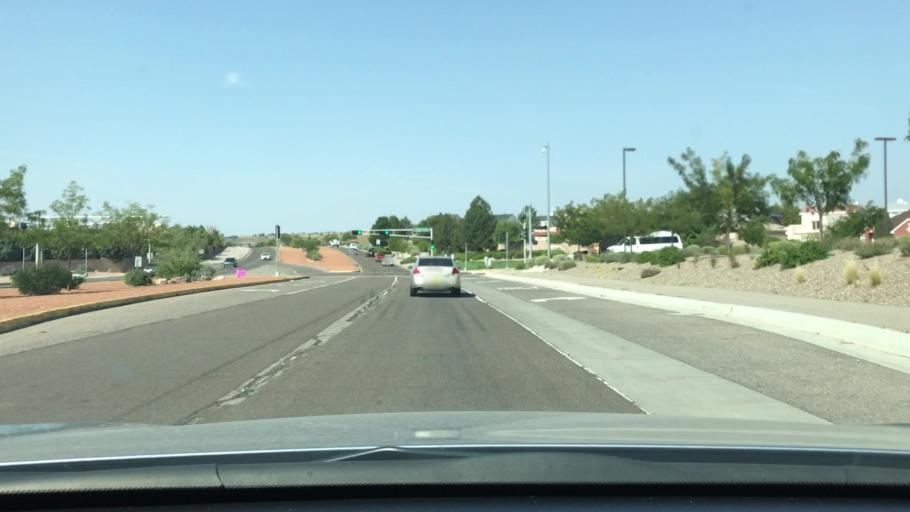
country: US
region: New Mexico
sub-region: Bernalillo County
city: Paradise Hills
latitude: 35.1814
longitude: -106.6804
